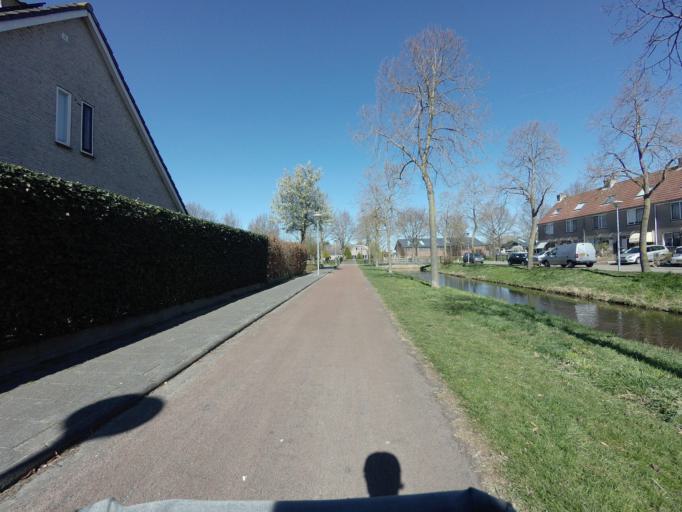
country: NL
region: Utrecht
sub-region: Gemeente Woerden
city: Woerden
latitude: 52.0818
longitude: 4.8567
